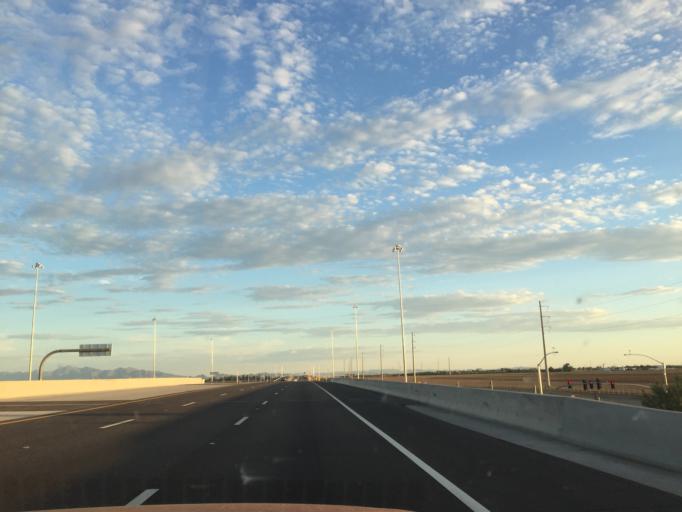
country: US
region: Arizona
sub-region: Maricopa County
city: Citrus Park
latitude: 33.5816
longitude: -112.4184
